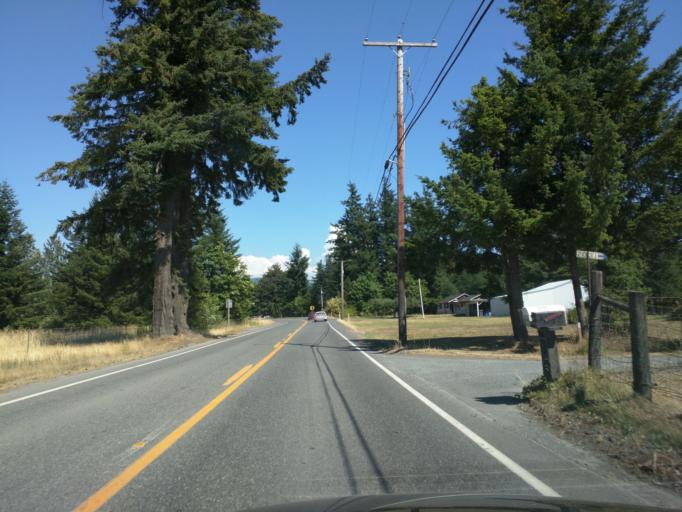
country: US
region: Washington
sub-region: Whatcom County
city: Everson
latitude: 48.8913
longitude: -122.3798
